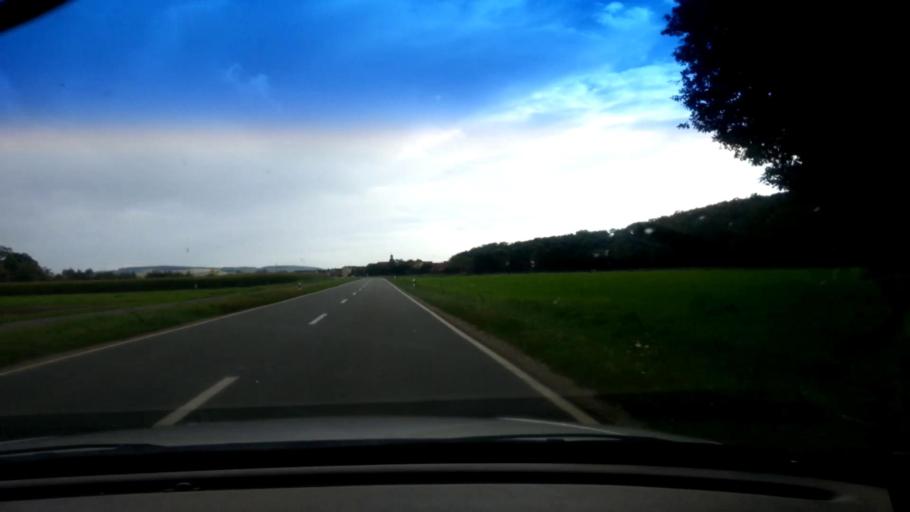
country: DE
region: Bavaria
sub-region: Upper Franconia
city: Ebensfeld
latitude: 50.0716
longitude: 10.9423
